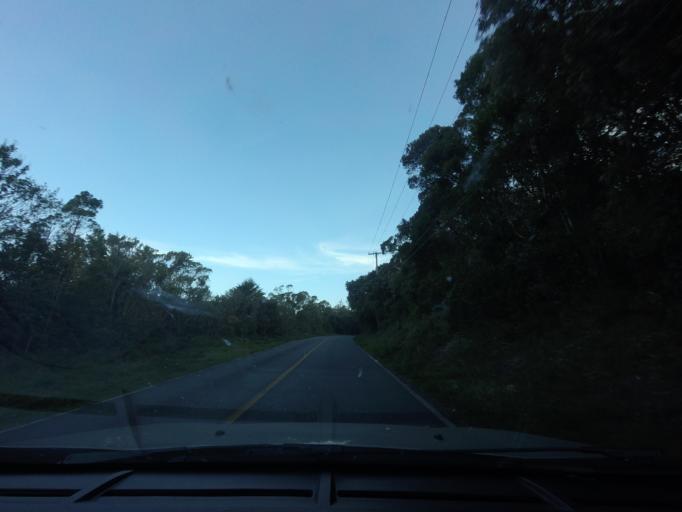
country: BR
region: Sao Paulo
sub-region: Campos Do Jordao
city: Campos do Jordao
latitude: -22.7657
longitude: -45.5450
